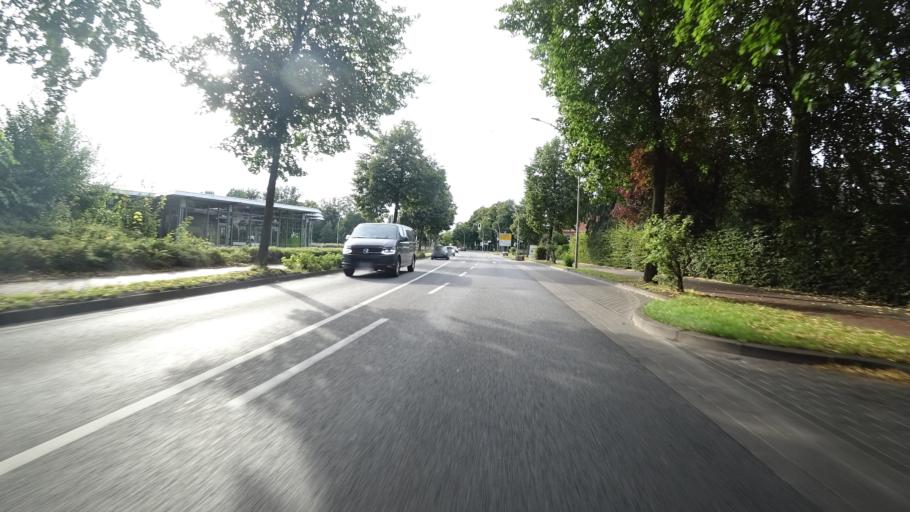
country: DE
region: North Rhine-Westphalia
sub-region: Regierungsbezirk Detmold
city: Harsewinkel
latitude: 51.9595
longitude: 8.2221
